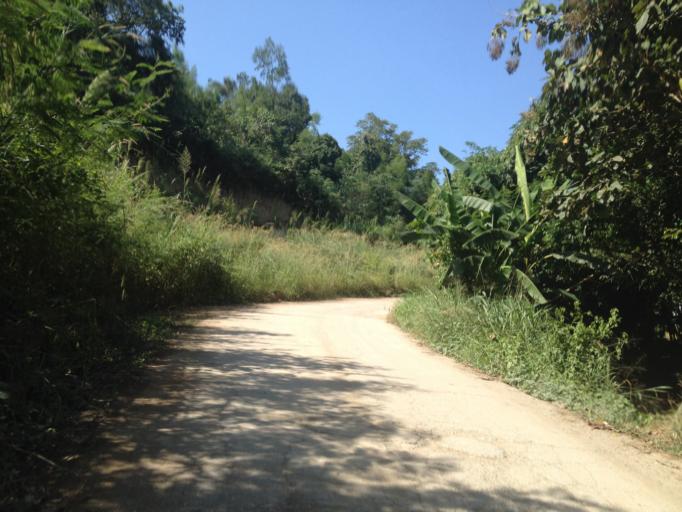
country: TH
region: Chiang Mai
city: Hang Dong
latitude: 18.7442
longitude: 98.8896
